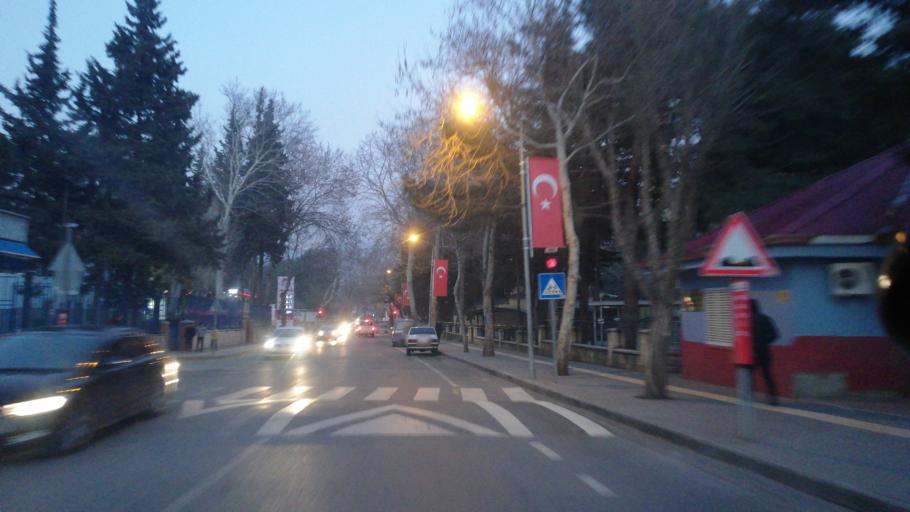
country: TR
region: Kahramanmaras
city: Kahramanmaras
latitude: 37.5885
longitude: 36.9194
